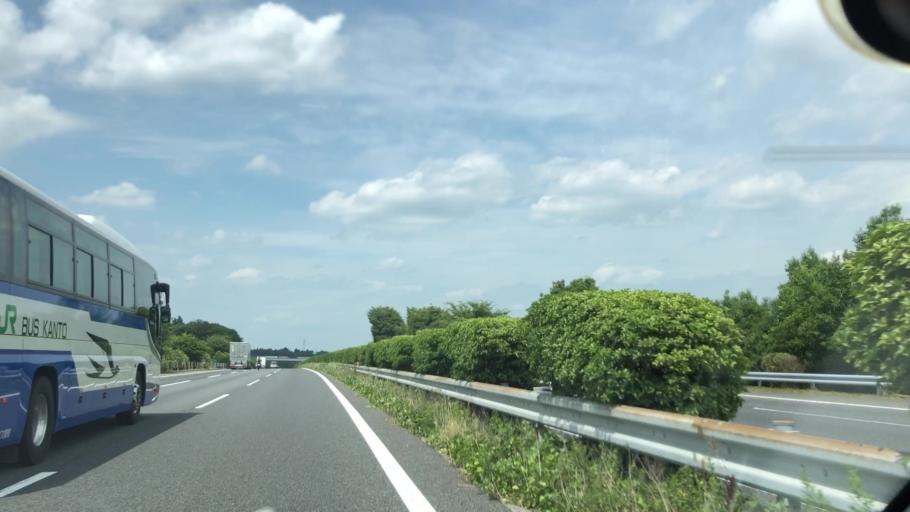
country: JP
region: Tochigi
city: Kanuma
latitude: 36.5076
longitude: 139.7686
